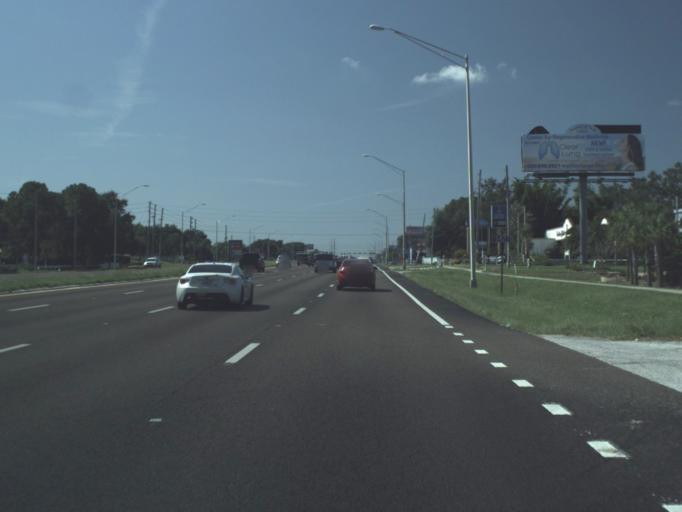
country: US
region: Florida
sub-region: Pinellas County
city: Palm Harbor
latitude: 28.0844
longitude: -82.7395
